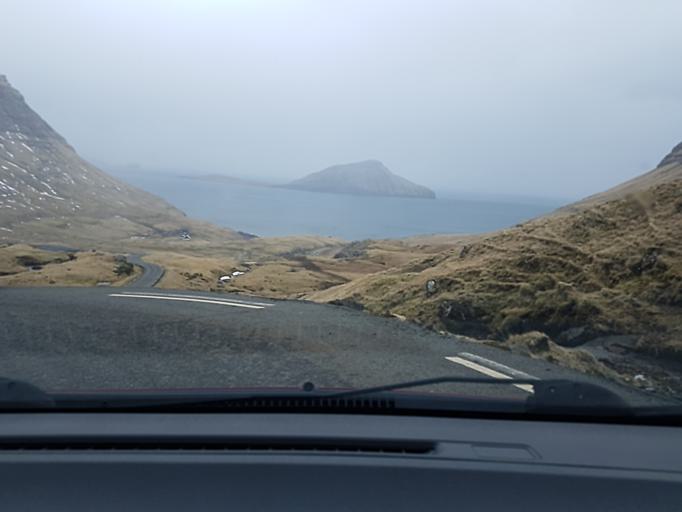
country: FO
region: Streymoy
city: Kollafjordhur
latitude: 62.0499
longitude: -6.9225
